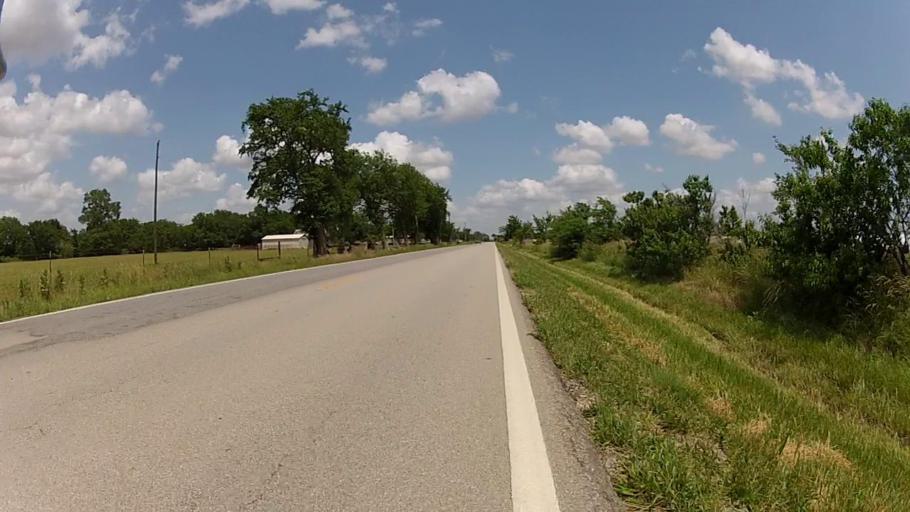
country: US
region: Kansas
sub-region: Labette County
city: Altamont
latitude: 37.1931
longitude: -95.3186
